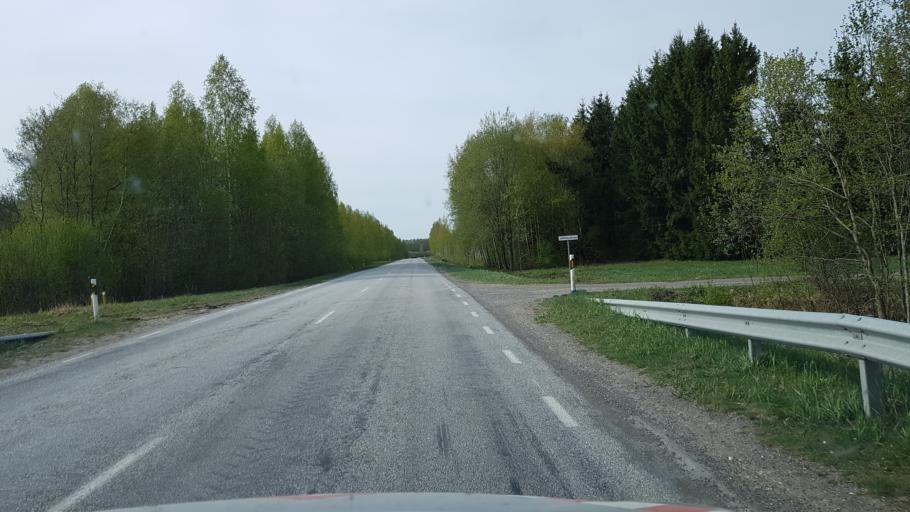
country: EE
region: Paernumaa
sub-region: Audru vald
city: Audru
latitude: 58.4107
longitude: 24.3086
